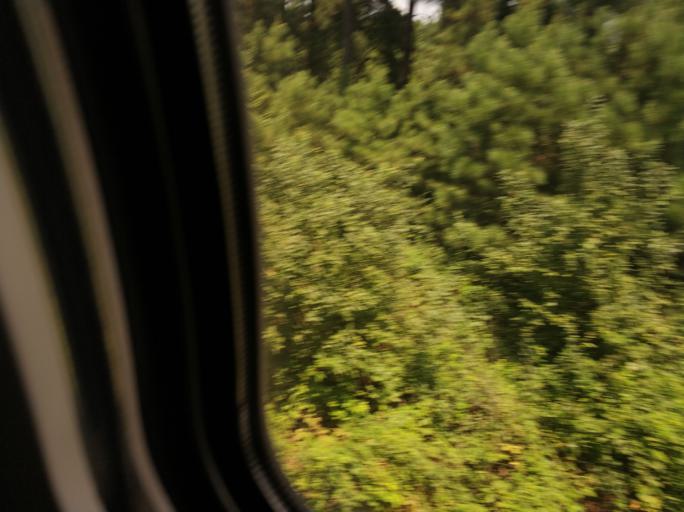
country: IR
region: Gilan
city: Rasht
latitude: 37.1859
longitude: 49.6031
